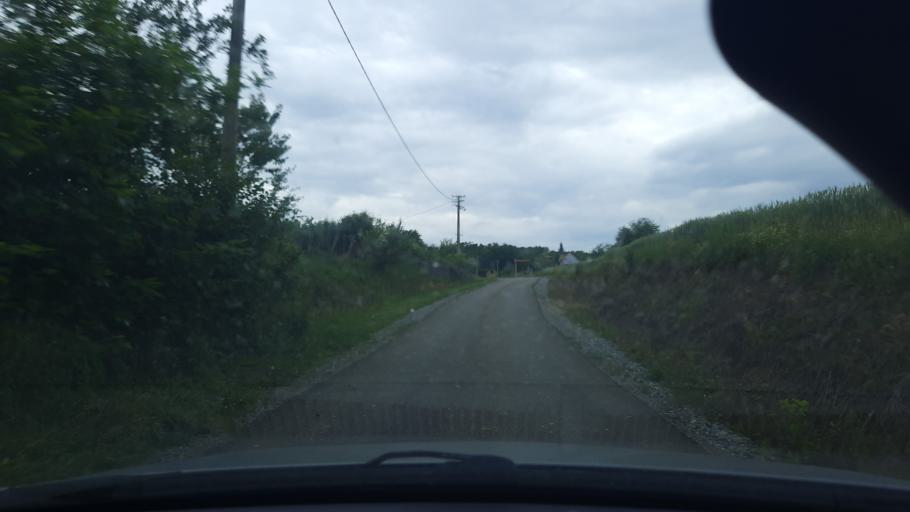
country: RS
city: Jarebice
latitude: 44.4901
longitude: 19.4792
